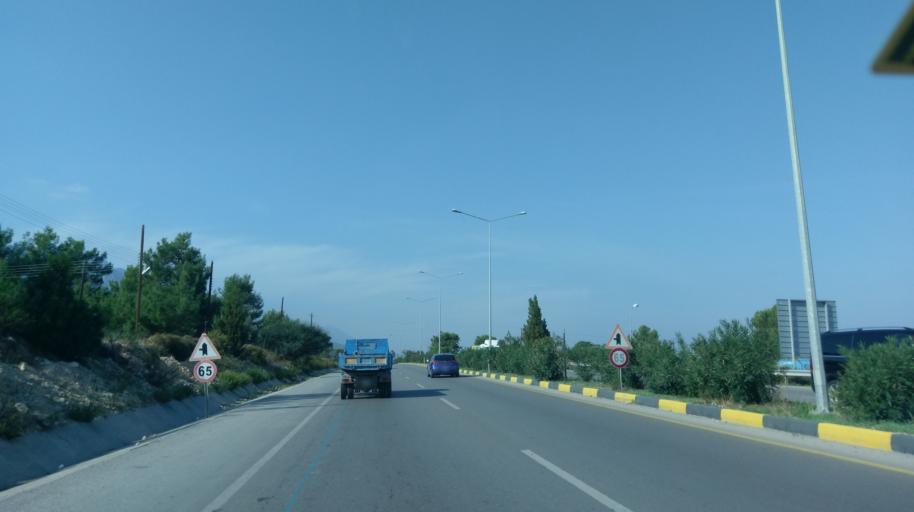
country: CY
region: Keryneia
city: Kyrenia
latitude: 35.3282
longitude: 33.2953
